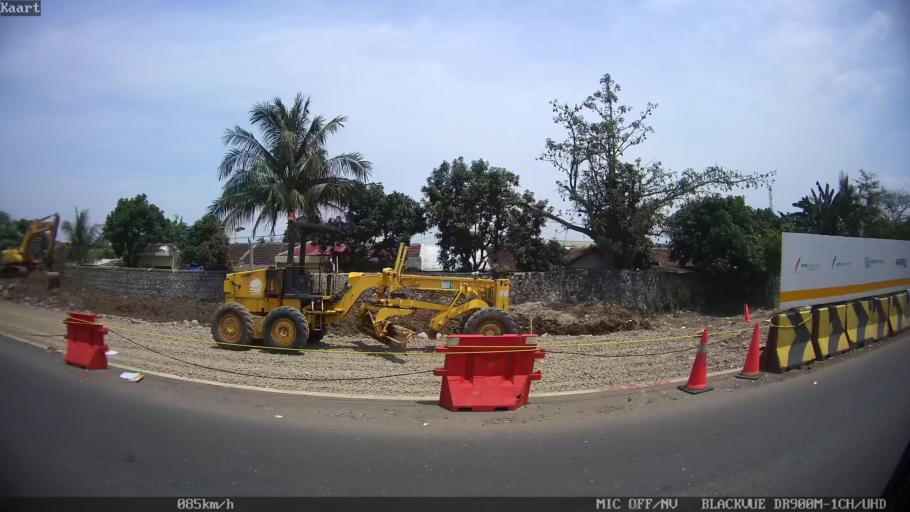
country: ID
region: Banten
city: Serang
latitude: -6.1385
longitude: 106.2315
